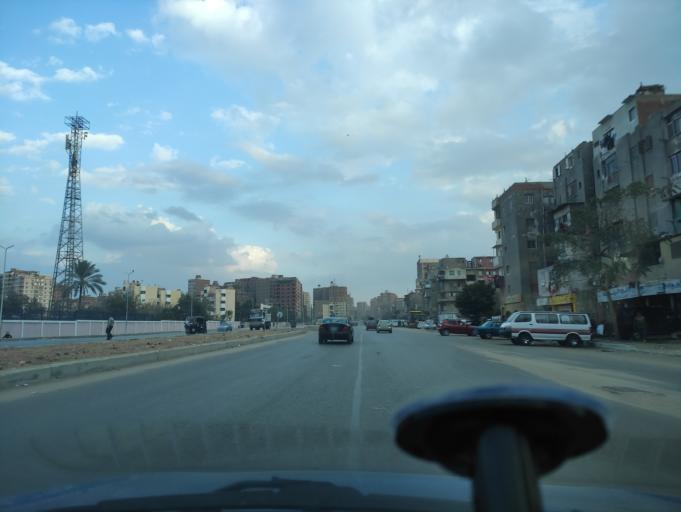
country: EG
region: Muhafazat al Qalyubiyah
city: Al Khankah
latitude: 30.1355
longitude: 31.3533
